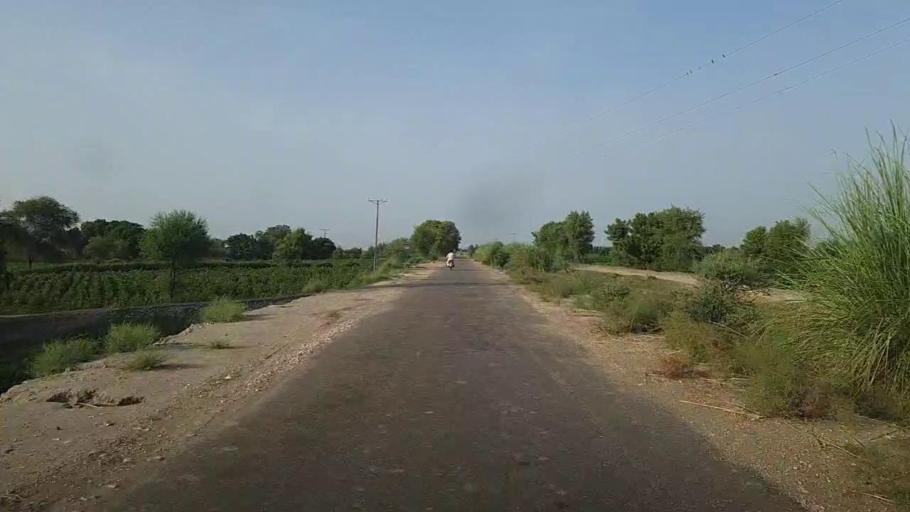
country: PK
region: Sindh
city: Khairpur
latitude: 28.0843
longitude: 69.8161
